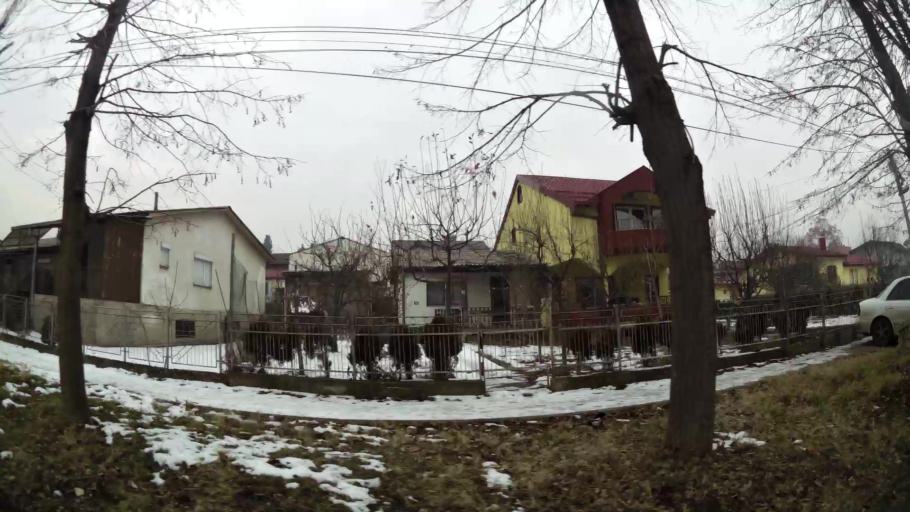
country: MK
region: Cair
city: Cair
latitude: 42.0138
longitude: 21.4603
